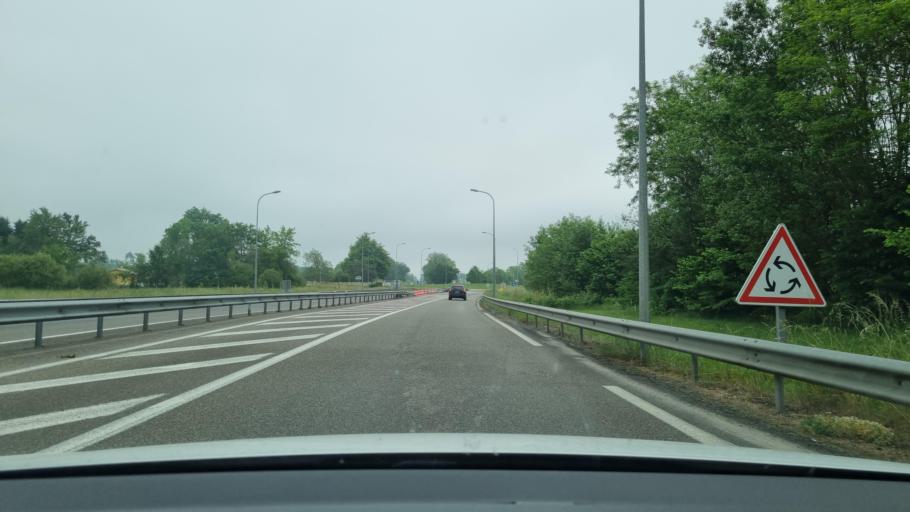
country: FR
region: Aquitaine
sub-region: Departement des Landes
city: Benquet
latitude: 43.8439
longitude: -0.5260
